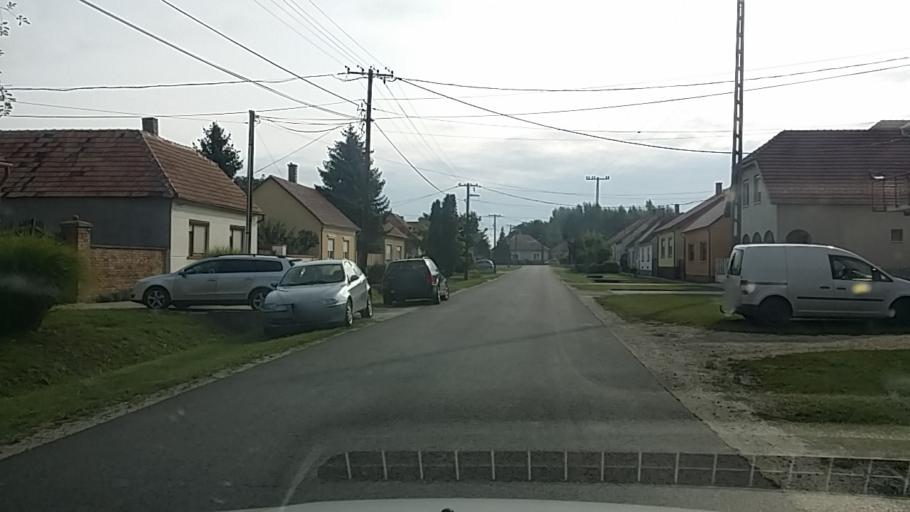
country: HU
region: Gyor-Moson-Sopron
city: Fertod
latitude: 47.6211
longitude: 16.8837
